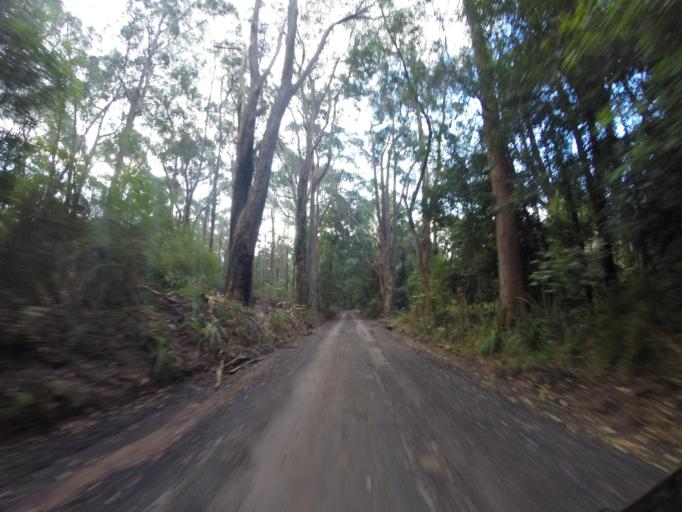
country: AU
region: New South Wales
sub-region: Wollongong
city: Cordeaux Heights
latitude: -34.4251
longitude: 150.7811
